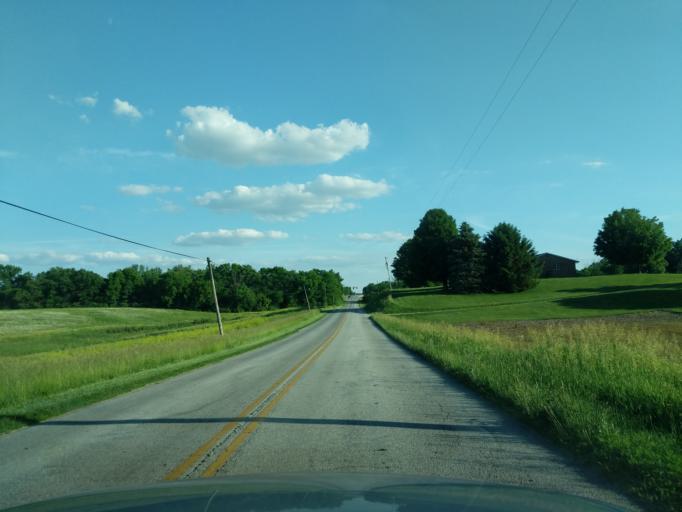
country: US
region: Indiana
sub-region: Huntington County
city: Huntington
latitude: 40.9051
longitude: -85.4714
